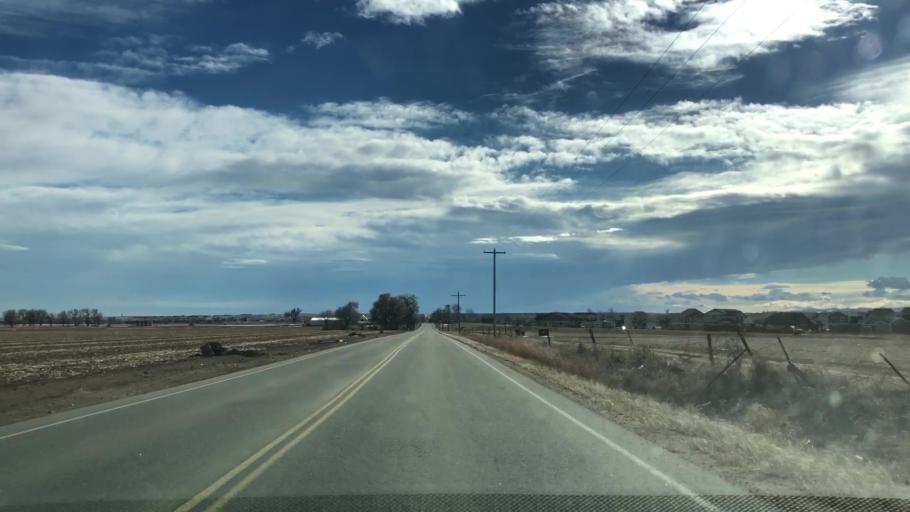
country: US
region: Colorado
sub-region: Weld County
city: Windsor
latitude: 40.5171
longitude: -104.9443
